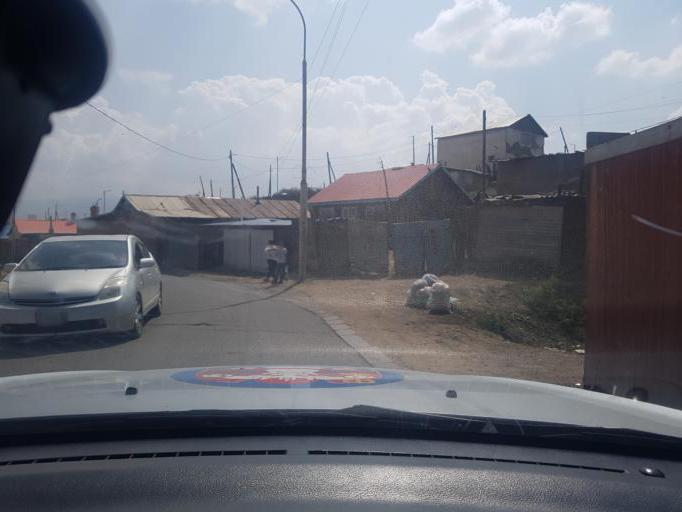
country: MN
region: Ulaanbaatar
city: Ulaanbaatar
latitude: 47.9384
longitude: 106.8982
